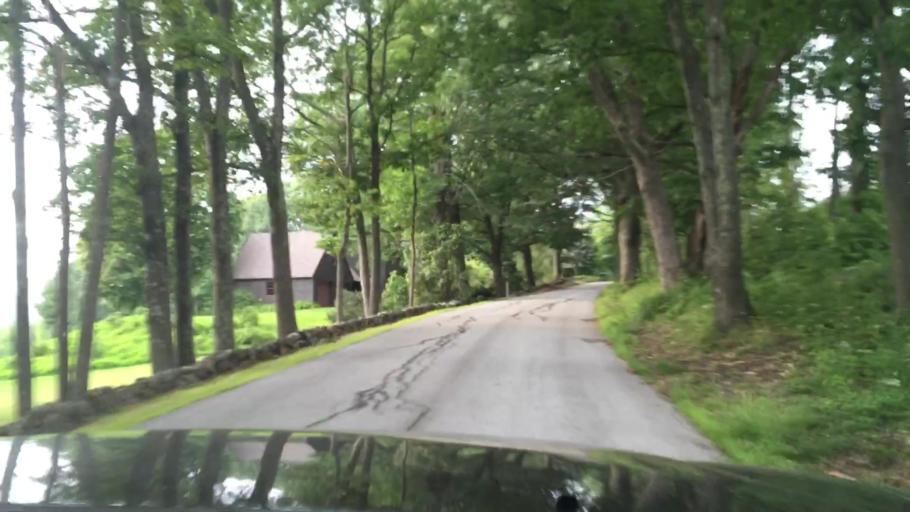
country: US
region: New Hampshire
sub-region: Belknap County
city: Meredith
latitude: 43.6958
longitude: -71.5097
